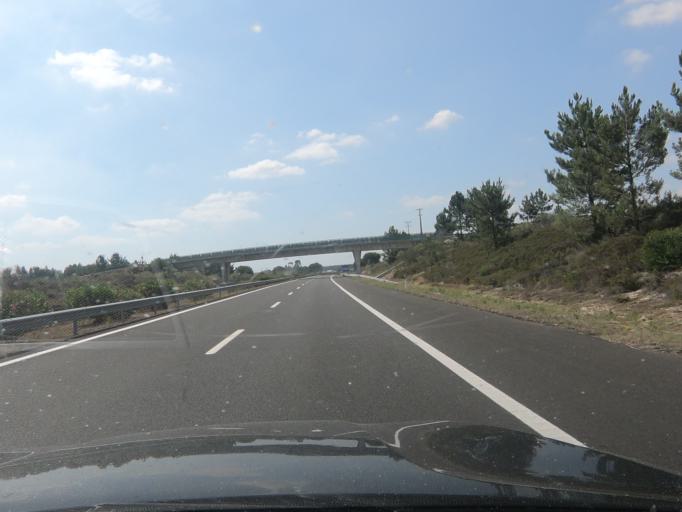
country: PT
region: Santarem
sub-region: Benavente
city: Poceirao
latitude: 38.7207
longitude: -8.6625
